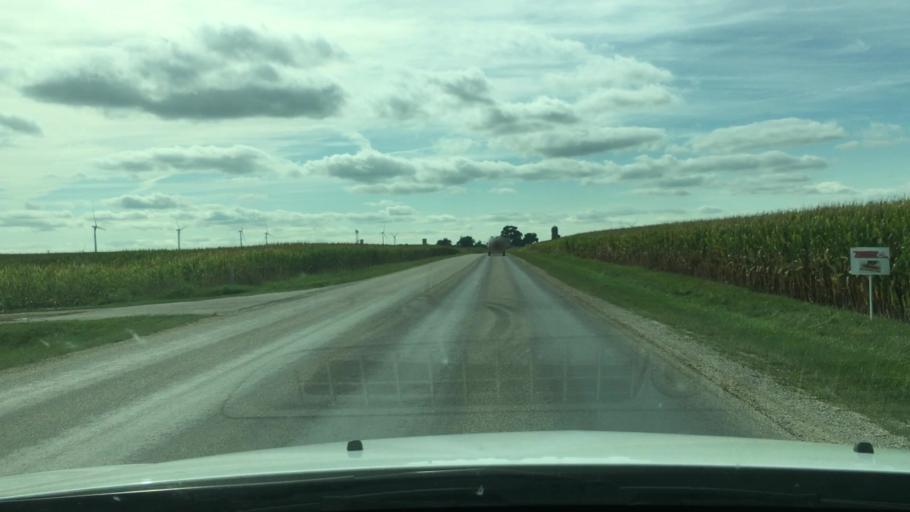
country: US
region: Illinois
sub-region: DeKalb County
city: Malta
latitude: 41.8493
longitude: -88.8873
